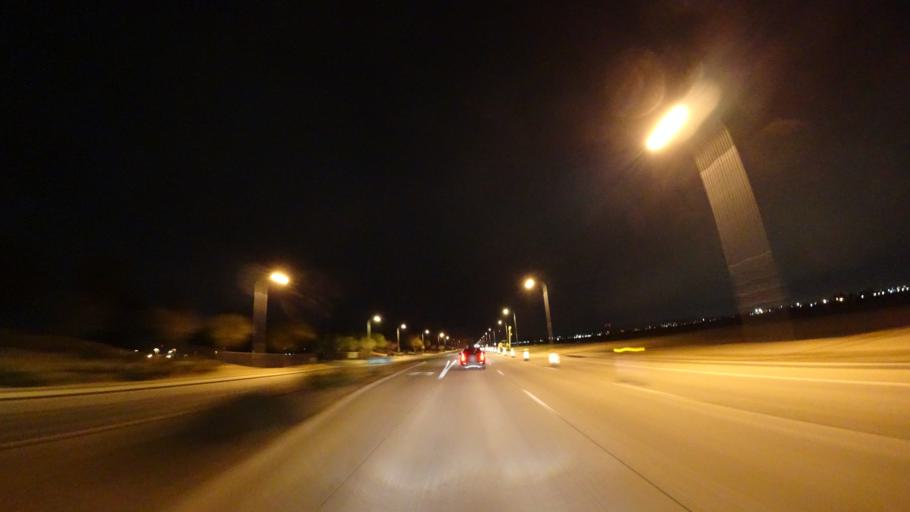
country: US
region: Arizona
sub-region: Maricopa County
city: Chandler
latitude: 33.2625
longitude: -111.8255
